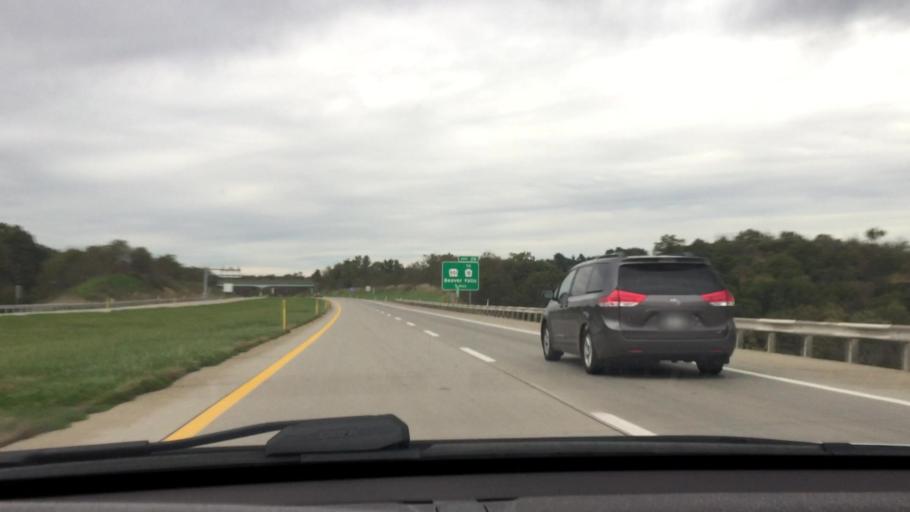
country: US
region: Pennsylvania
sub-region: Beaver County
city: West Mayfield
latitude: 40.7758
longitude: -80.3568
